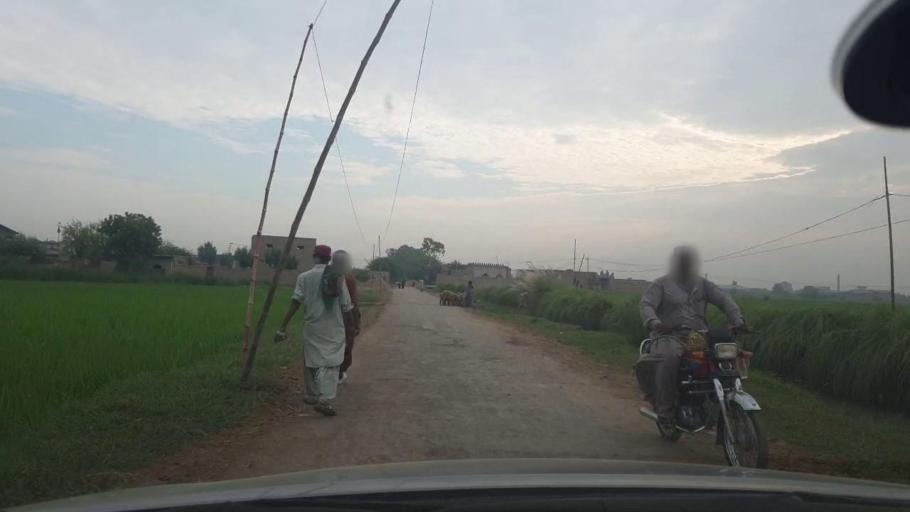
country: PK
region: Sindh
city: Jacobabad
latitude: 28.2928
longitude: 68.4198
